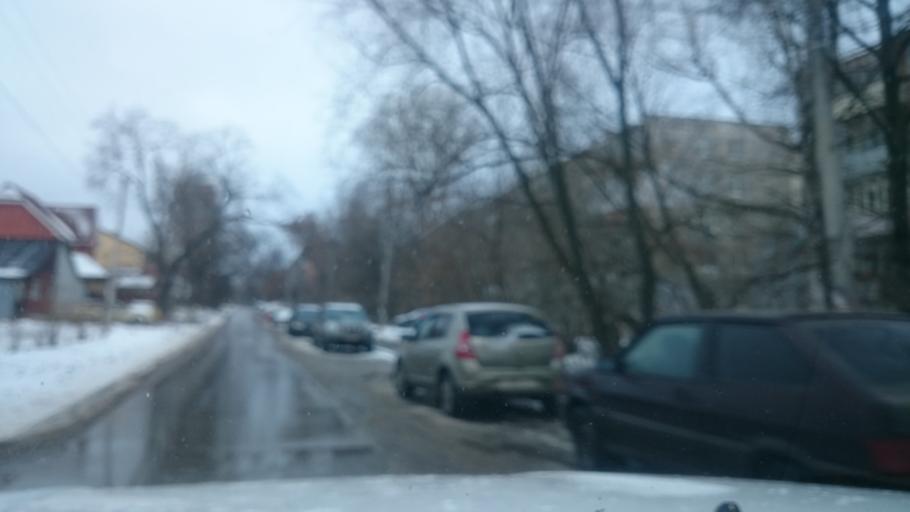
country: RU
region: Tula
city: Mendeleyevskiy
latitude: 54.1806
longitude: 37.5694
